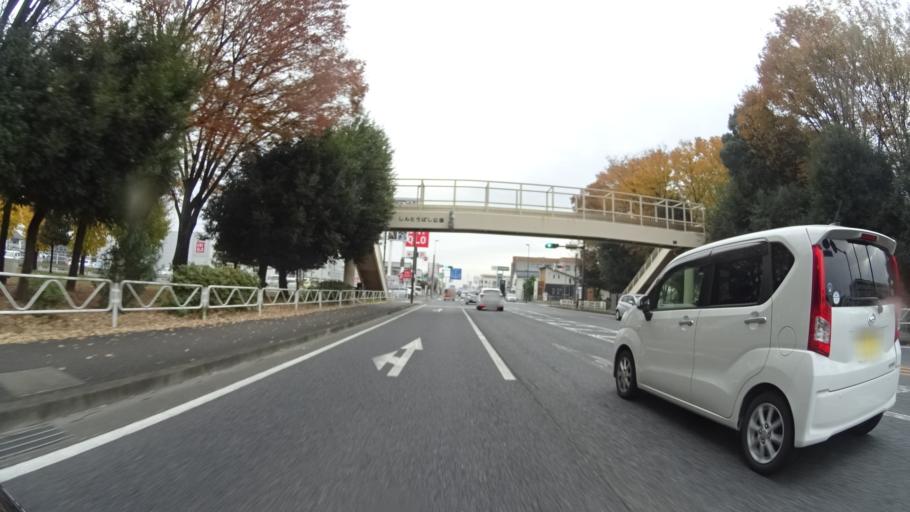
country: JP
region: Gunma
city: Maebashi-shi
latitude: 36.3826
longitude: 139.0932
